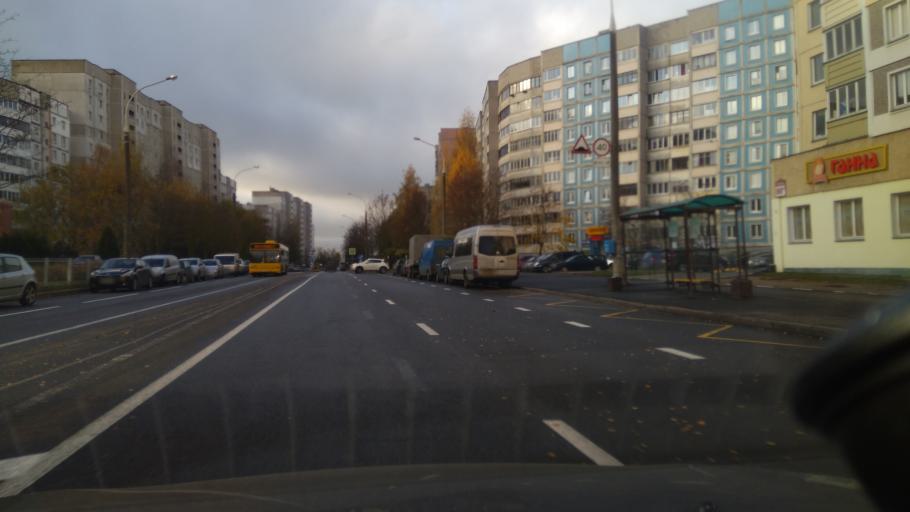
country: BY
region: Minsk
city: Malinovka
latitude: 53.8596
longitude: 27.4370
